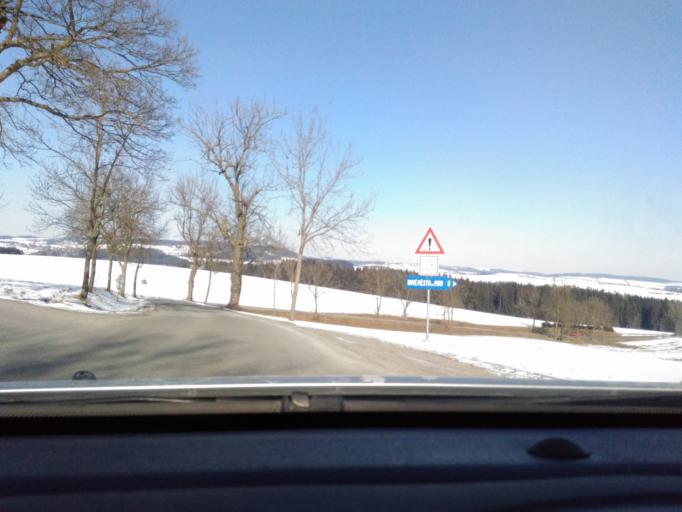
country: CZ
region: Vysocina
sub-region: Okres Zd'ar nad Sazavou
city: Nove Mesto na Morave
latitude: 49.5355
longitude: 16.0427
